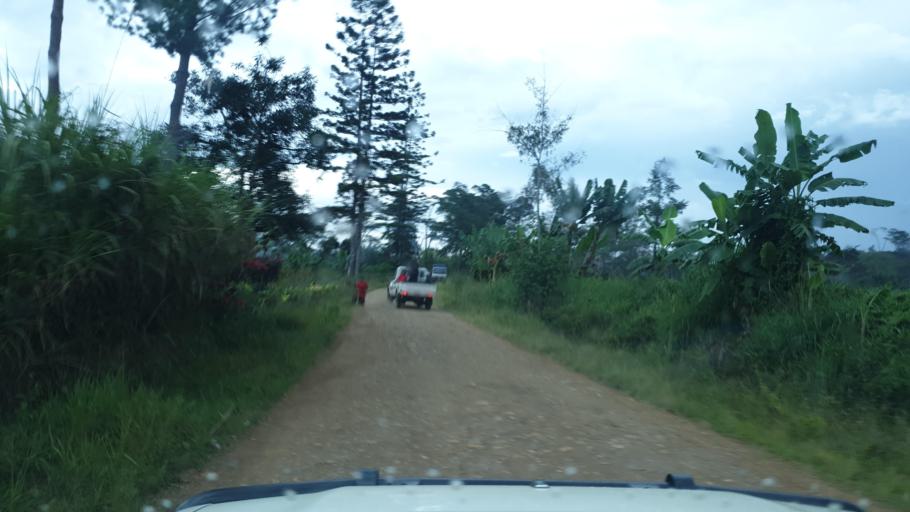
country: PG
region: Eastern Highlands
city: Goroka
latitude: -5.9829
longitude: 145.2817
